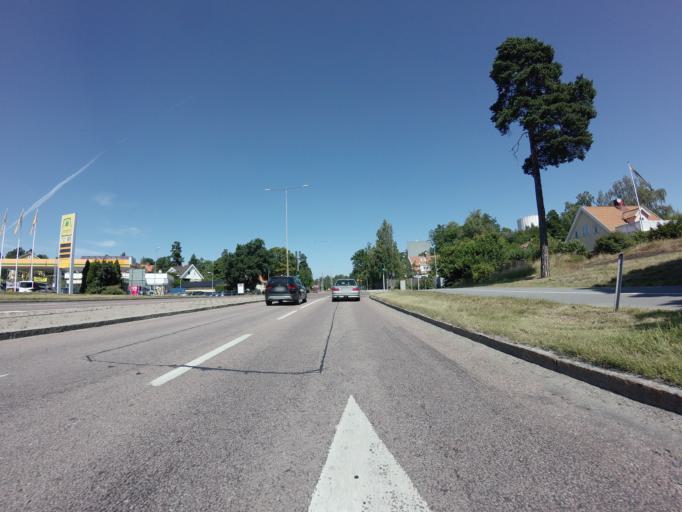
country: SE
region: Stockholm
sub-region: Lidingo
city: Lidingoe
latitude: 59.3568
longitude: 18.1366
